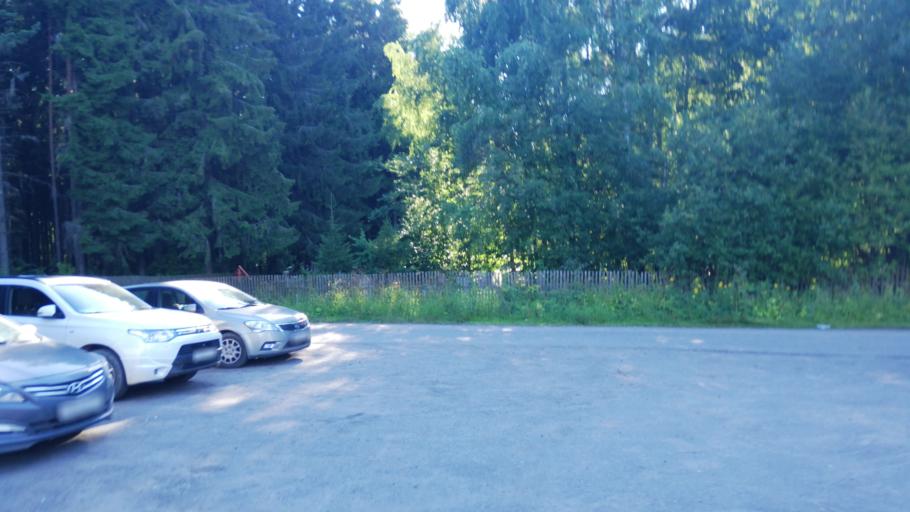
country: RU
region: Ivanovo
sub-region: Privolzhskiy Rayon
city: Ples
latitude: 57.4613
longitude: 41.4970
